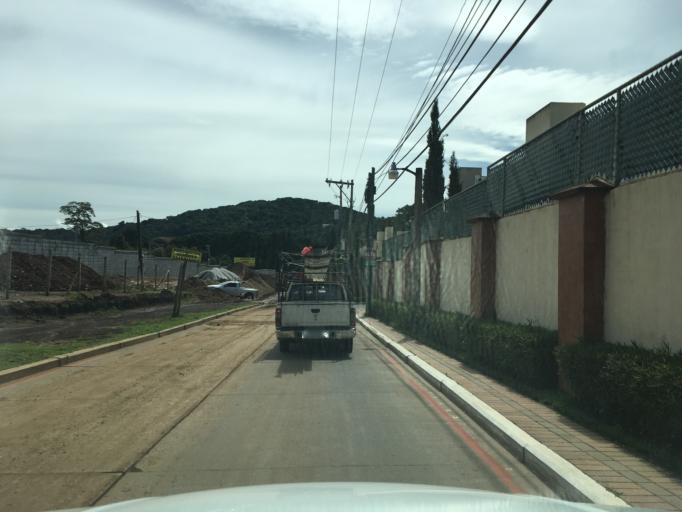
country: GT
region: Guatemala
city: Mixco
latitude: 14.6530
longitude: -90.5660
